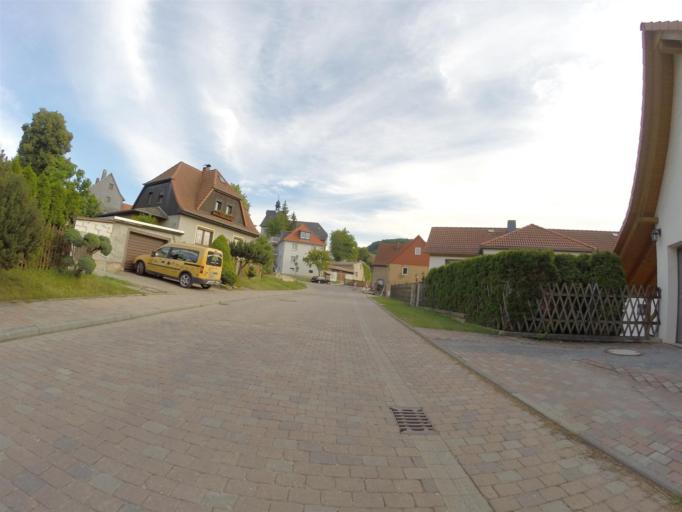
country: DE
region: Thuringia
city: Golmsdorf
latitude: 50.9727
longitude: 11.6670
